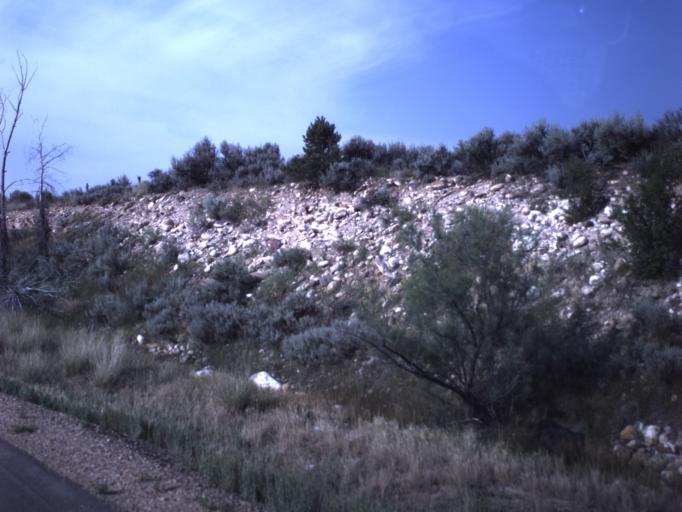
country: US
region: Utah
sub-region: Duchesne County
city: Duchesne
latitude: 40.3429
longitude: -110.4079
